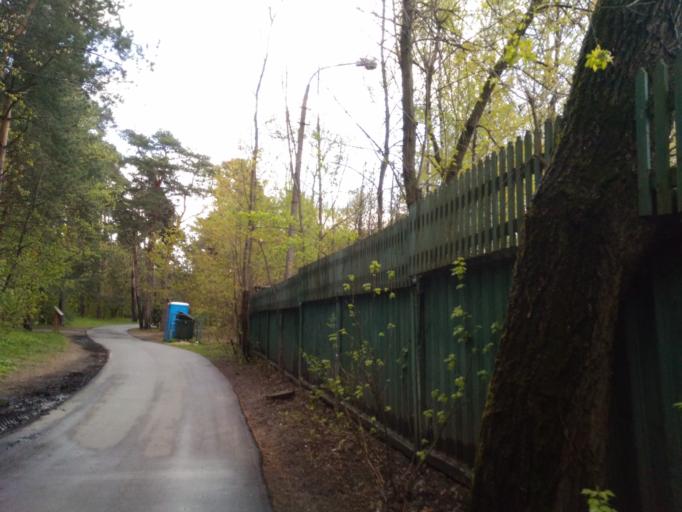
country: RU
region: Moscow
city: Shchukino
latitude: 55.7797
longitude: 37.4284
